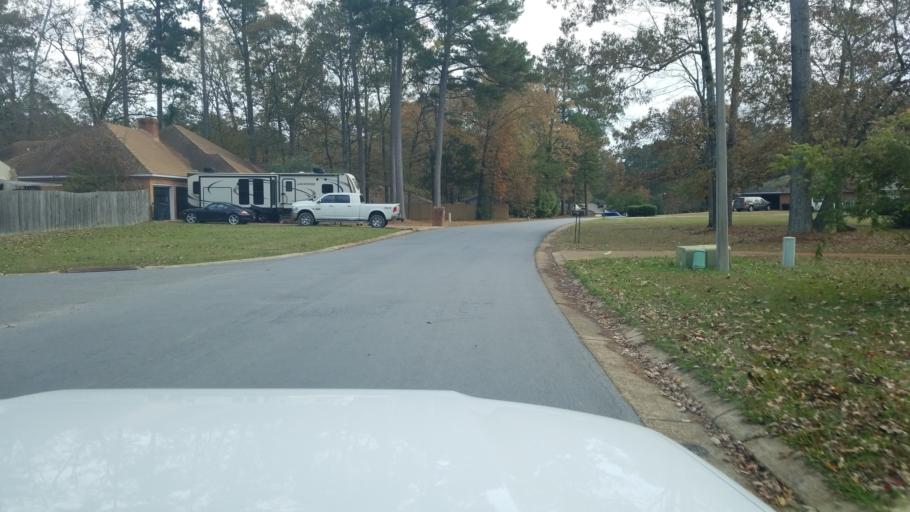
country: US
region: Mississippi
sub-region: Madison County
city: Ridgeland
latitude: 32.3864
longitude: -90.0341
